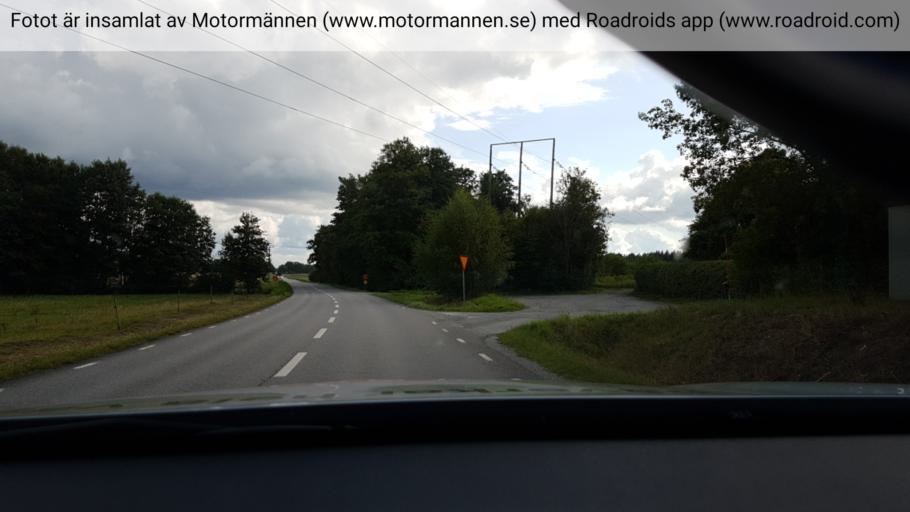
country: SE
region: Stockholm
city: Stenhamra
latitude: 59.3615
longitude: 17.7188
